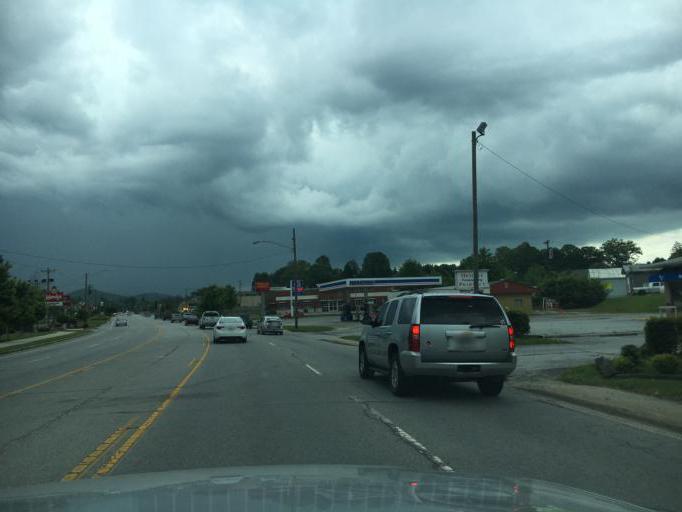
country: US
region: North Carolina
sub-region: Transylvania County
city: Brevard
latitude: 35.2431
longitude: -82.7248
